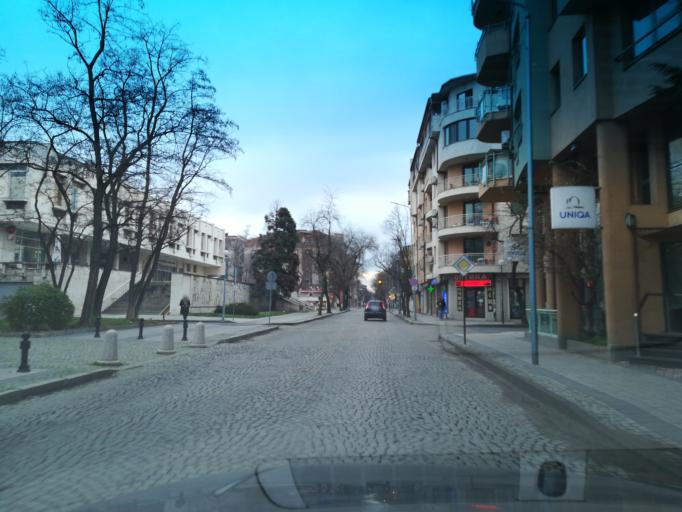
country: BG
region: Plovdiv
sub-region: Obshtina Plovdiv
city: Plovdiv
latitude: 42.1396
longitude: 24.7451
